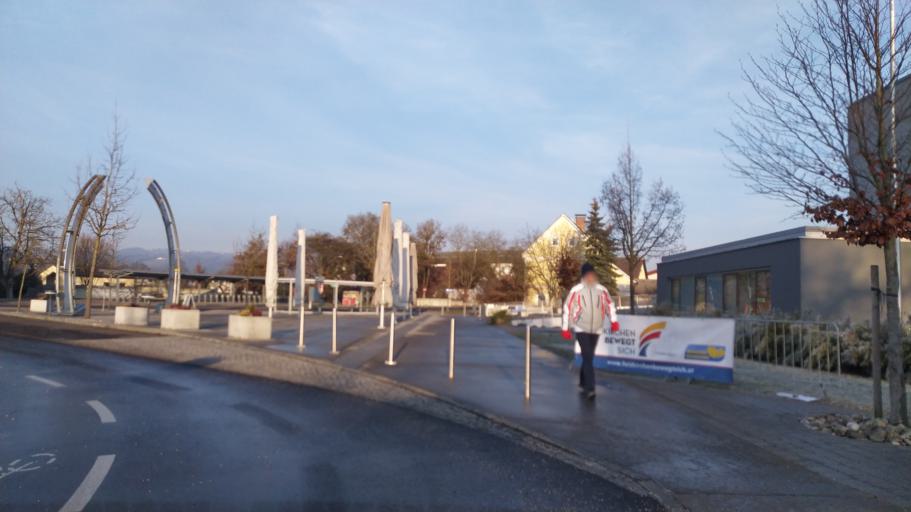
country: AT
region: Upper Austria
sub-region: Politischer Bezirk Urfahr-Umgebung
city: Feldkirchen an der Donau
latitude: 48.3456
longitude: 14.0546
